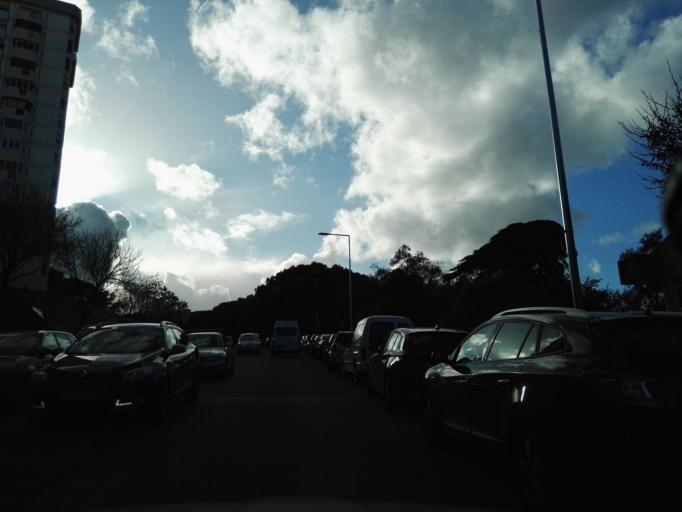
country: PT
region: Lisbon
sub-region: Loures
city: Moscavide
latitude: 38.7679
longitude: -9.1153
